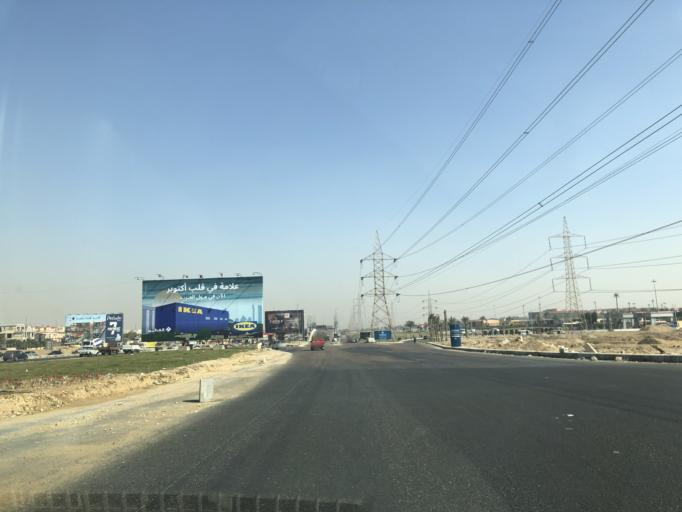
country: EG
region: Al Jizah
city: Madinat Sittah Uktubar
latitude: 29.9717
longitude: 31.0076
